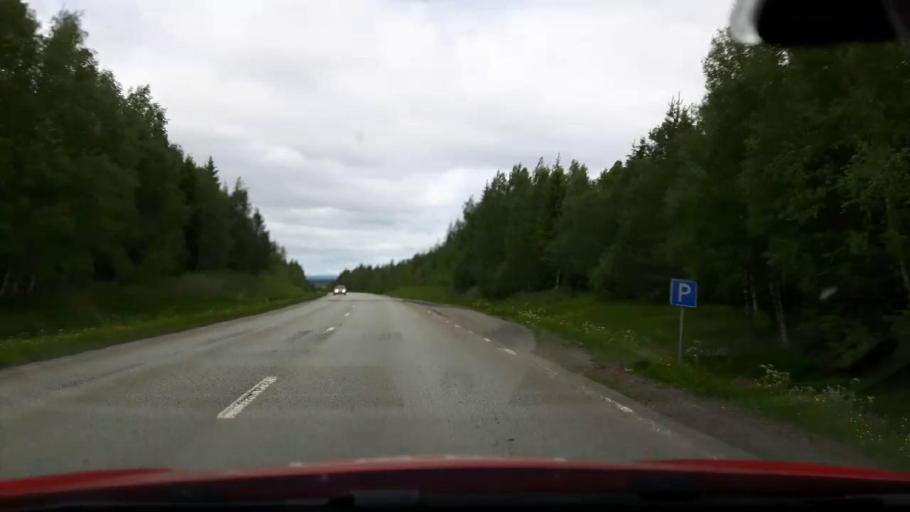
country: SE
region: Jaemtland
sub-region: Krokoms Kommun
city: Krokom
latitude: 63.3901
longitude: 14.5052
